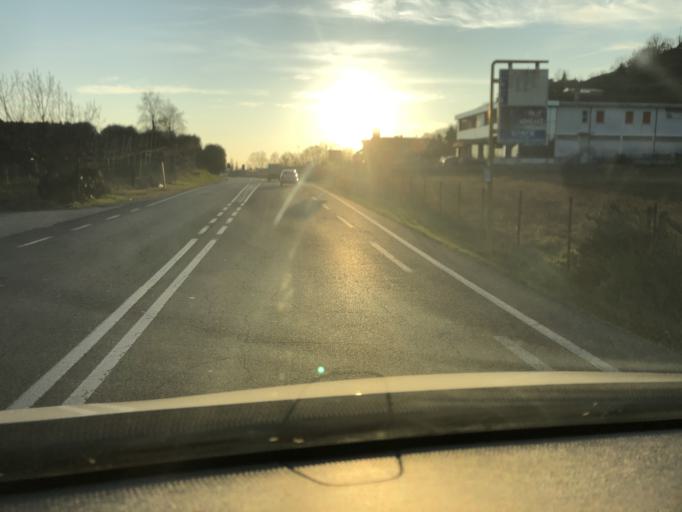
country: IT
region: Veneto
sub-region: Provincia di Verona
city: Pastrengo
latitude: 45.4842
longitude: 10.8082
